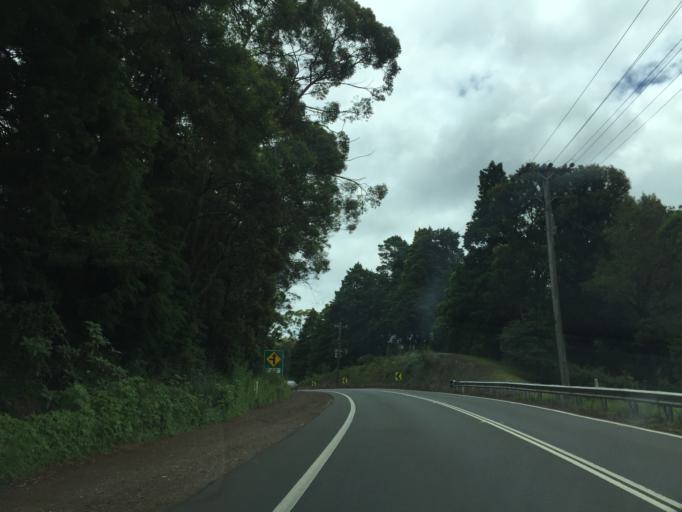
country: AU
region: New South Wales
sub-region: Hawkesbury
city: Richmond
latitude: -33.5197
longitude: 150.6278
